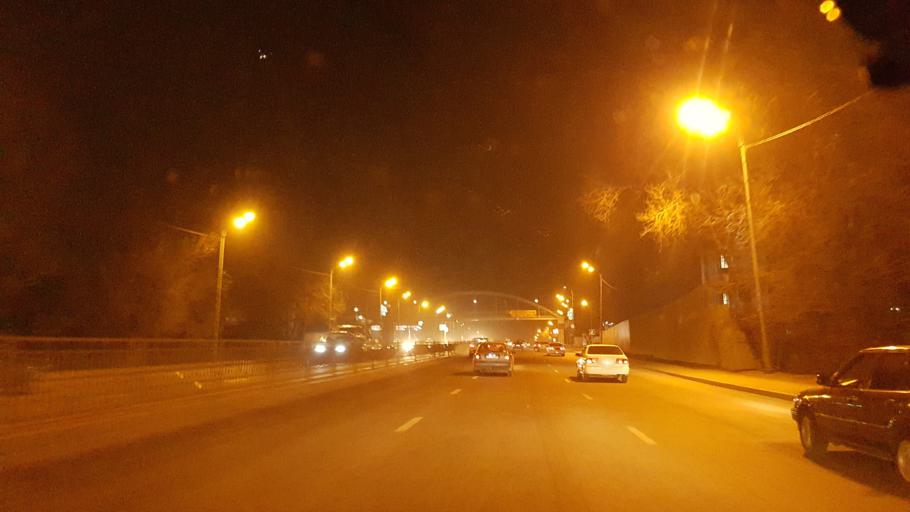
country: KZ
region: Almaty Qalasy
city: Almaty
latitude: 43.2683
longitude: 76.8750
